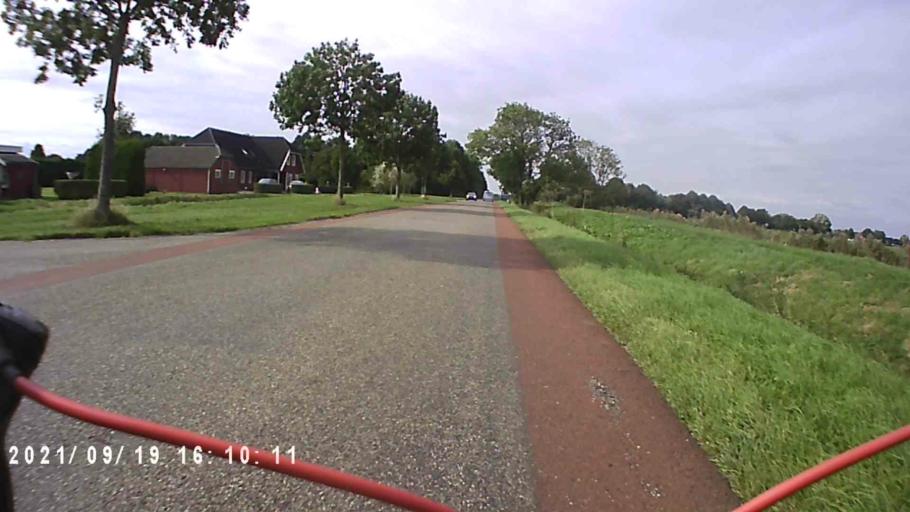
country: DE
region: Lower Saxony
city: Bunde
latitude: 53.1835
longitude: 7.2200
